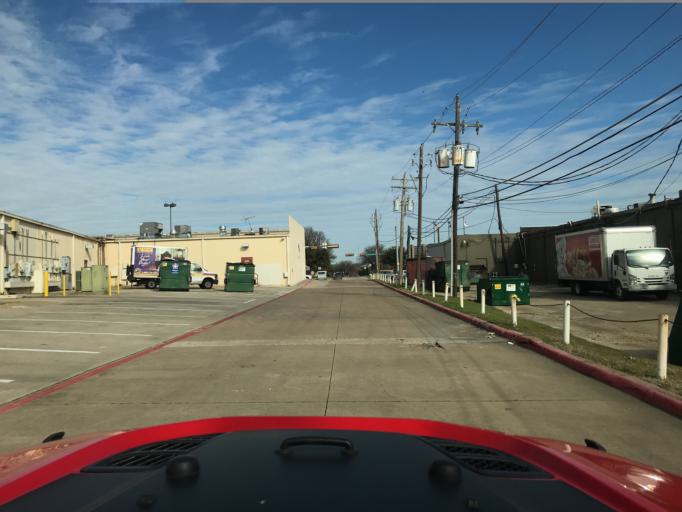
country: US
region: Texas
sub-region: Denton County
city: Lewisville
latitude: 33.0410
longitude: -97.0240
